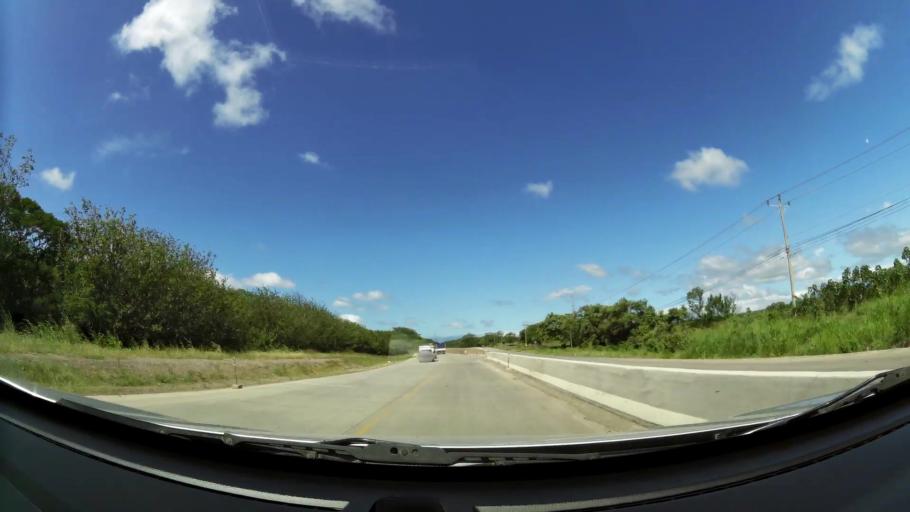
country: CR
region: Guanacaste
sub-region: Canton de Canas
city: Canas
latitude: 10.4352
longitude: -85.1054
